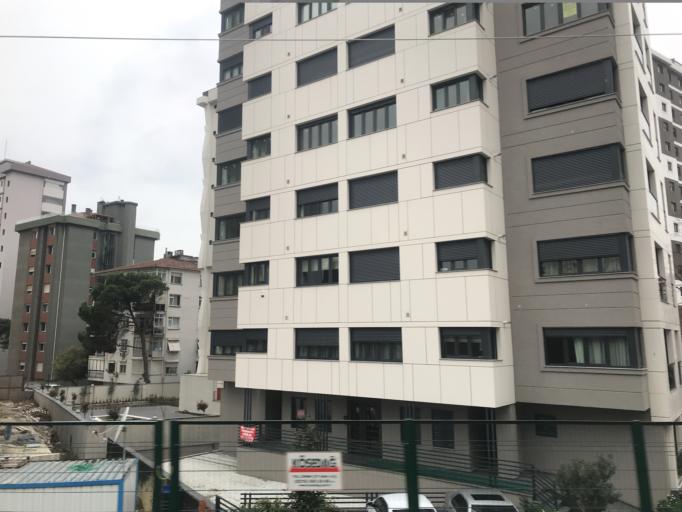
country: TR
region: Istanbul
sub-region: Atasehir
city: Atasehir
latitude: 40.9638
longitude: 29.0785
